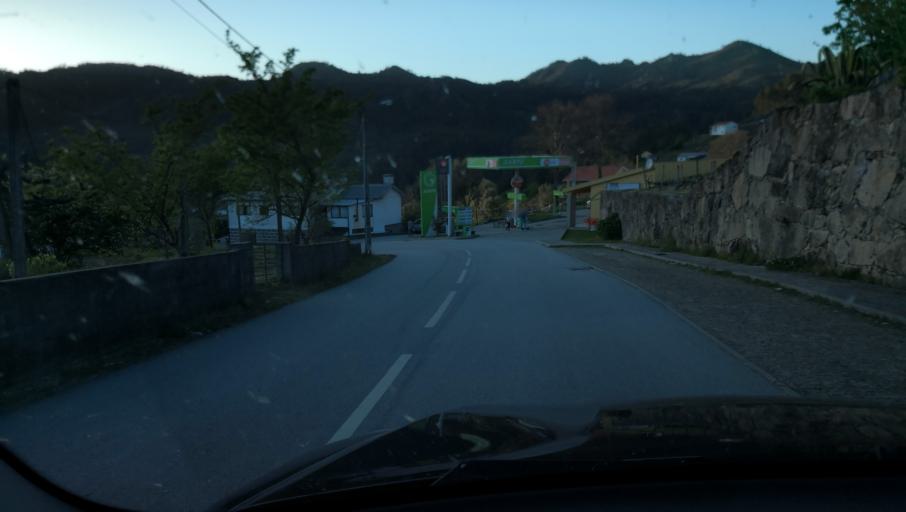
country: PT
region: Vila Real
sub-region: Mondim de Basto
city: Mondim de Basto
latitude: 41.4147
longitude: -7.8794
